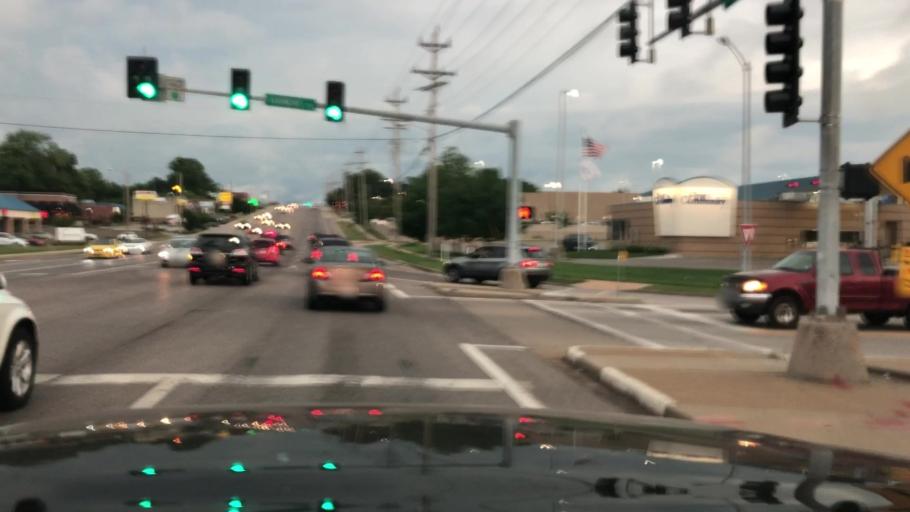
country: US
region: Missouri
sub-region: Saint Louis County
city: Bridgeton
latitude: 38.7467
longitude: -90.4206
